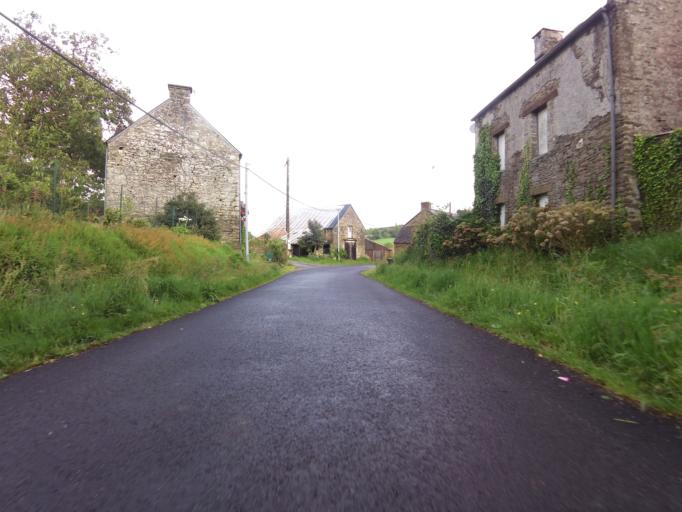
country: FR
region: Brittany
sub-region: Departement du Morbihan
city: Pluherlin
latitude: 47.7116
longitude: -2.3569
